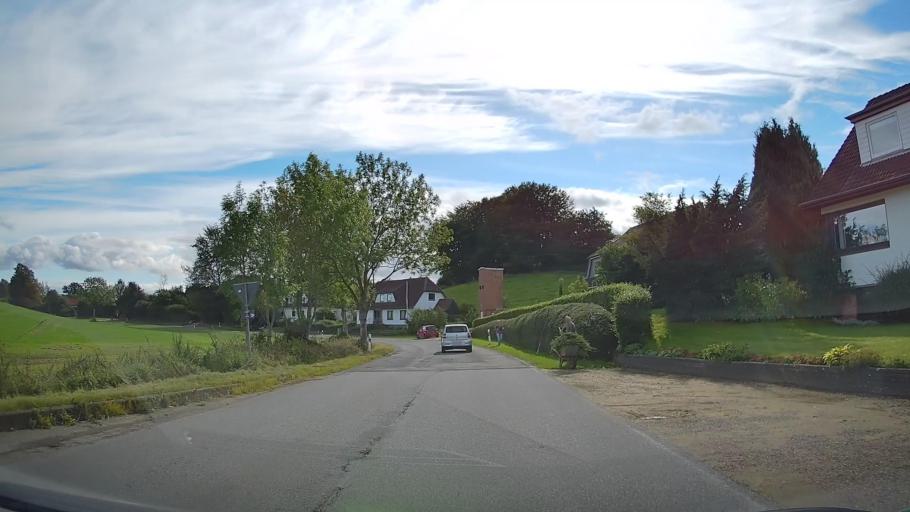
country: DE
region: Schleswig-Holstein
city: Glucksburg
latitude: 54.8432
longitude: 9.5833
